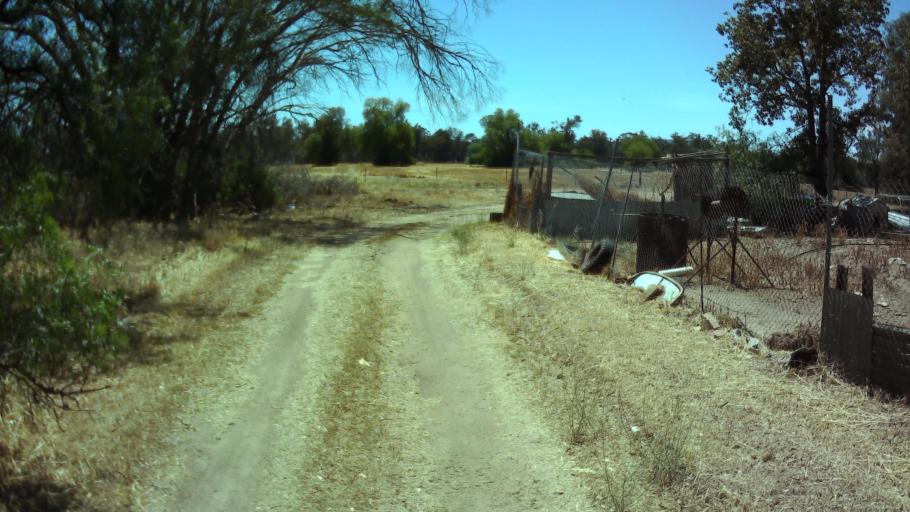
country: AU
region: New South Wales
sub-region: Weddin
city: Grenfell
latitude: -34.0356
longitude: 147.9287
